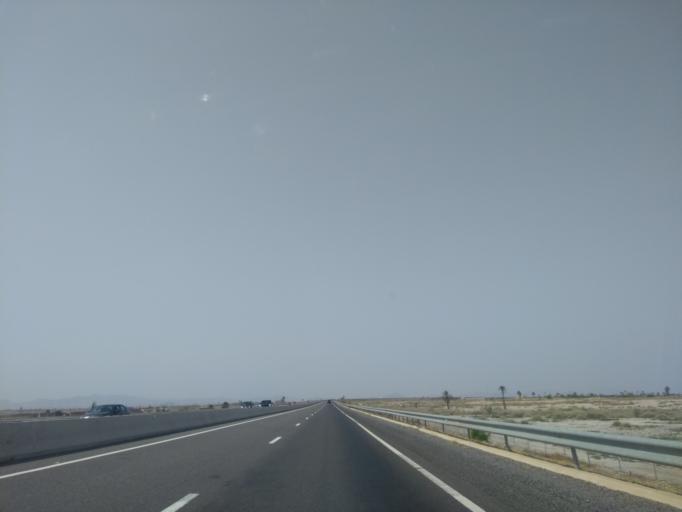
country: MA
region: Marrakech-Tensift-Al Haouz
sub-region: Marrakech
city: Marrakesh
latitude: 31.6580
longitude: -8.2951
